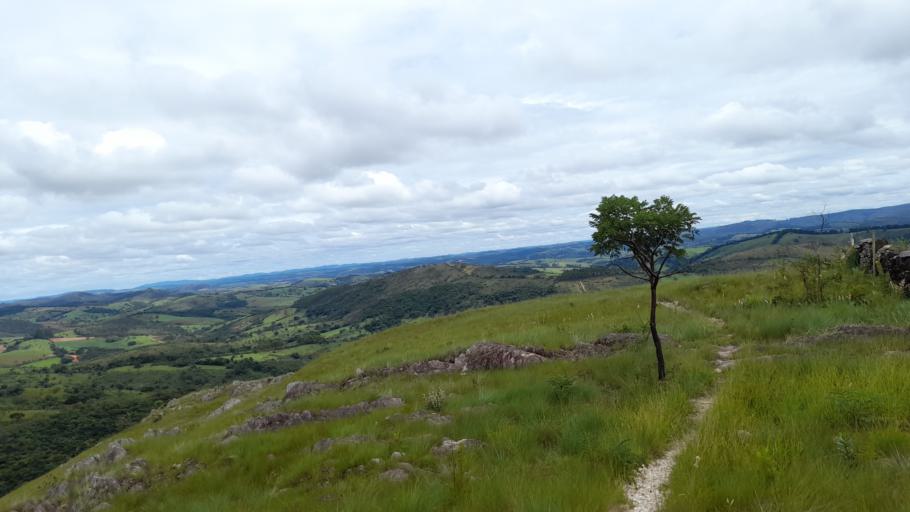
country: BR
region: Minas Gerais
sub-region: Sao Joao Del Rei
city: Sao Joao del Rei
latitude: -21.1182
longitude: -44.2871
